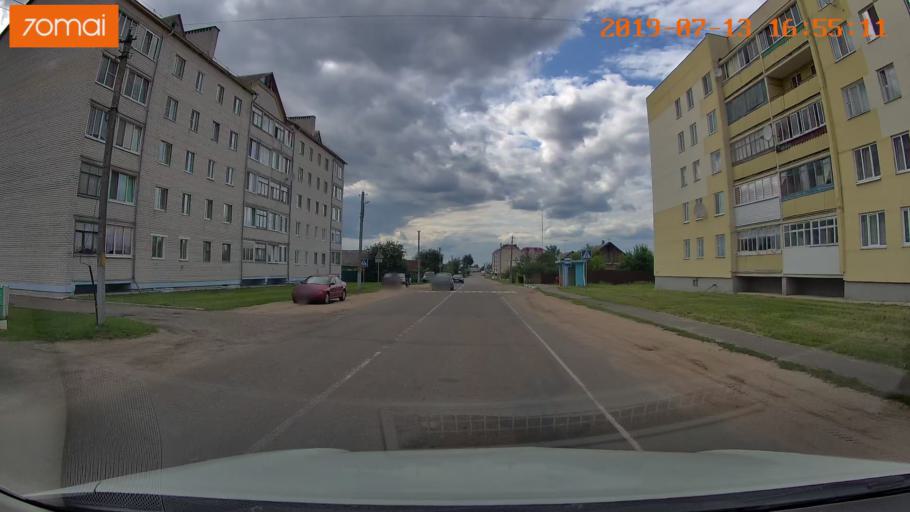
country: BY
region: Mogilev
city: Kirawsk
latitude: 53.2664
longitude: 29.4698
